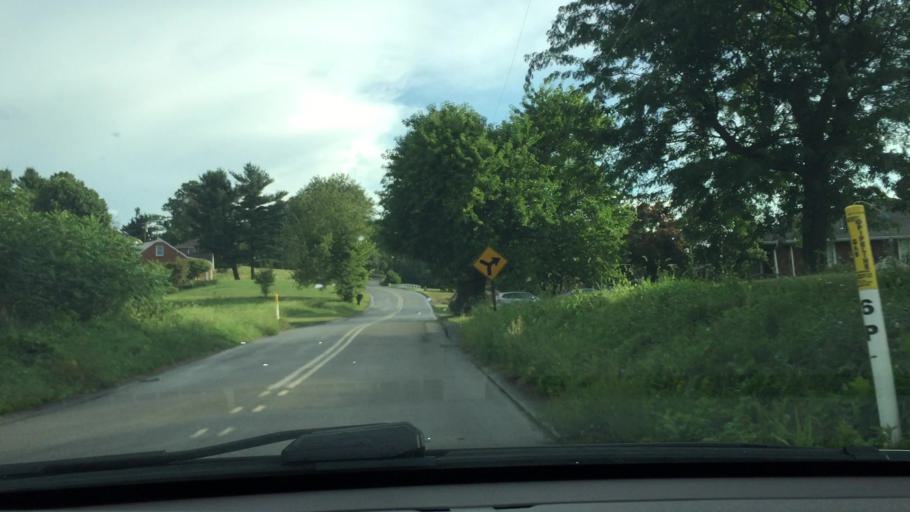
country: US
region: Pennsylvania
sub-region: Washington County
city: McGovern
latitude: 40.2098
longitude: -80.1857
